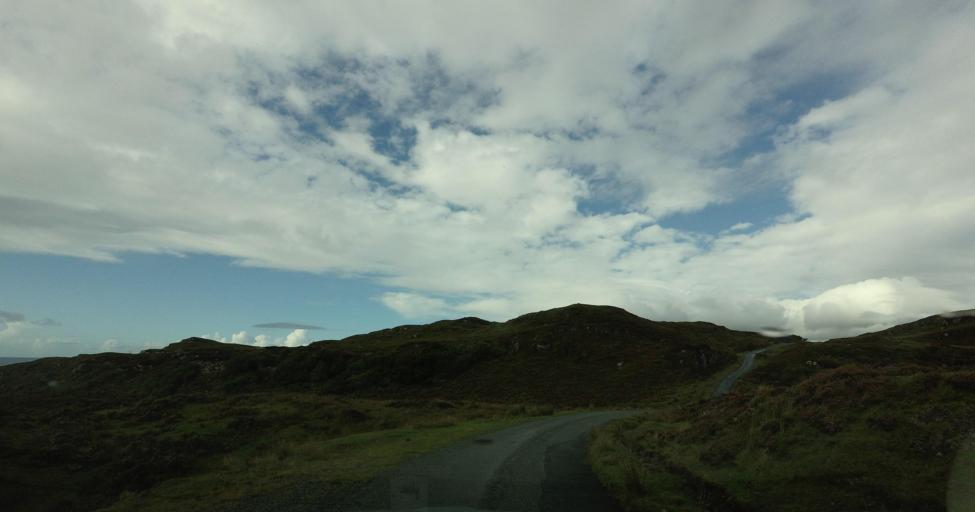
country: GB
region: Scotland
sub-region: Highland
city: Isle of Skye
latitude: 57.1429
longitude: -6.0891
